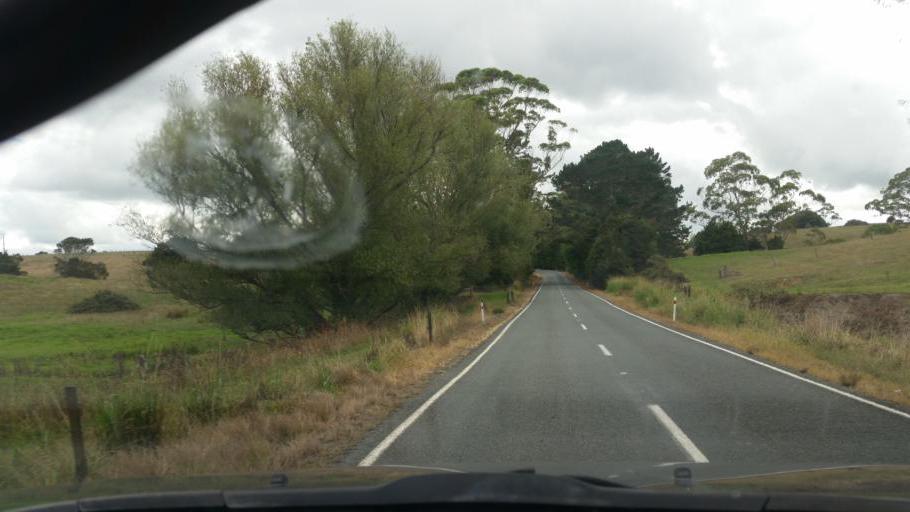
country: NZ
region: Northland
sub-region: Whangarei
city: Ruakaka
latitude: -35.9882
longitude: 174.2931
